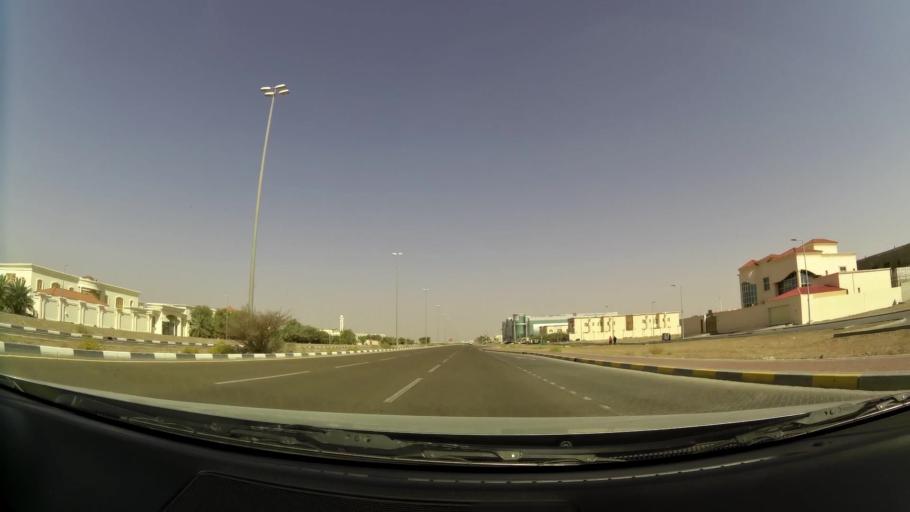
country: OM
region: Al Buraimi
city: Al Buraymi
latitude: 24.3421
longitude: 55.7969
